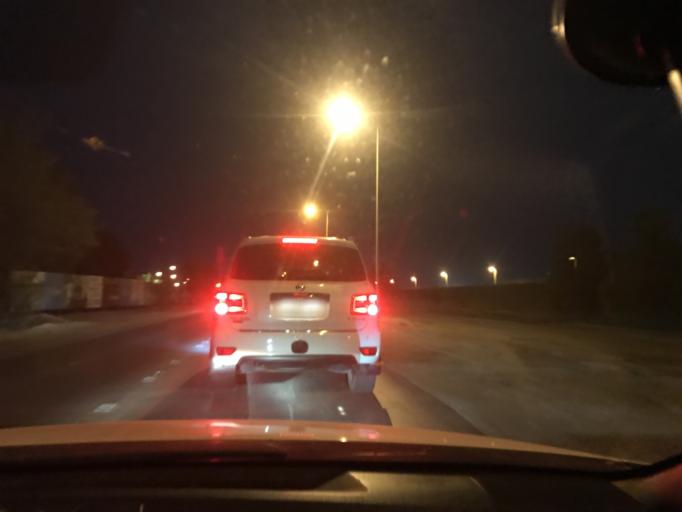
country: BH
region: Muharraq
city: Al Muharraq
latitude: 26.2812
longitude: 50.6200
